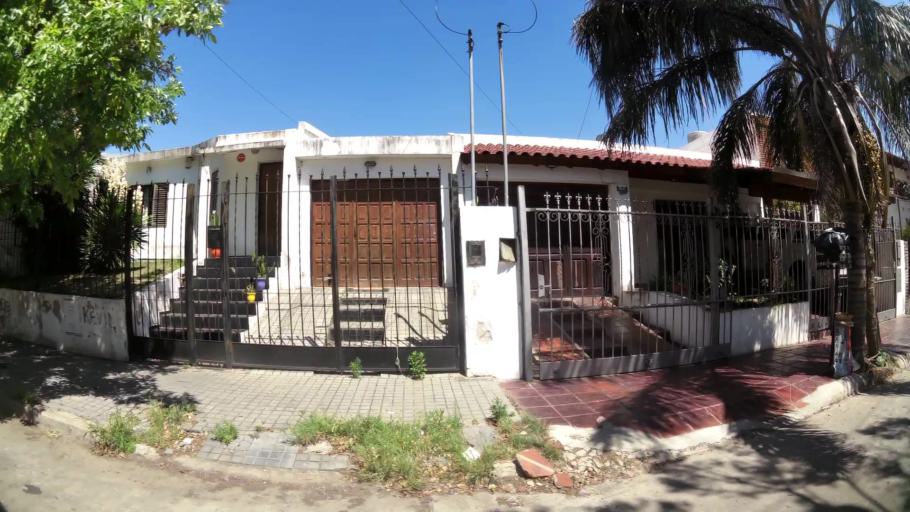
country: AR
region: Cordoba
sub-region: Departamento de Capital
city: Cordoba
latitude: -31.4266
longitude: -64.2034
